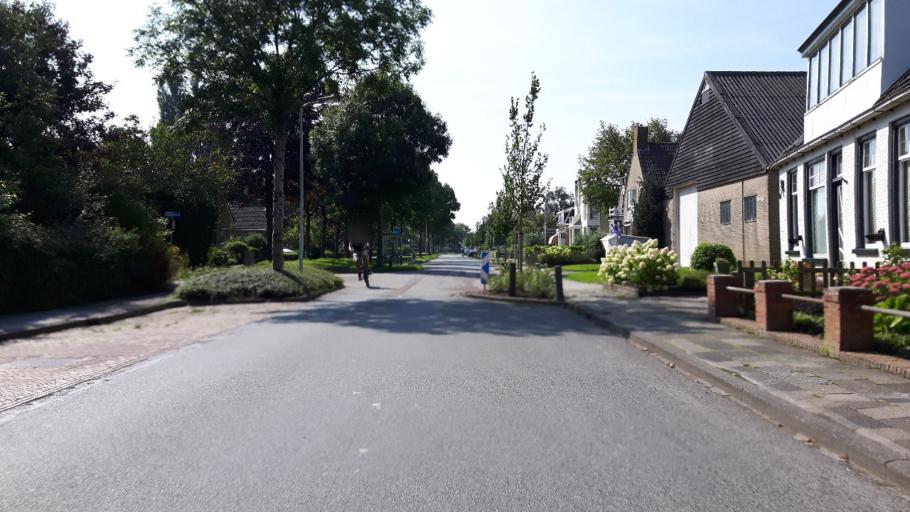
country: NL
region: Friesland
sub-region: Gemeente Ferwerderadiel
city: Marrum
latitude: 53.3256
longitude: 5.8029
